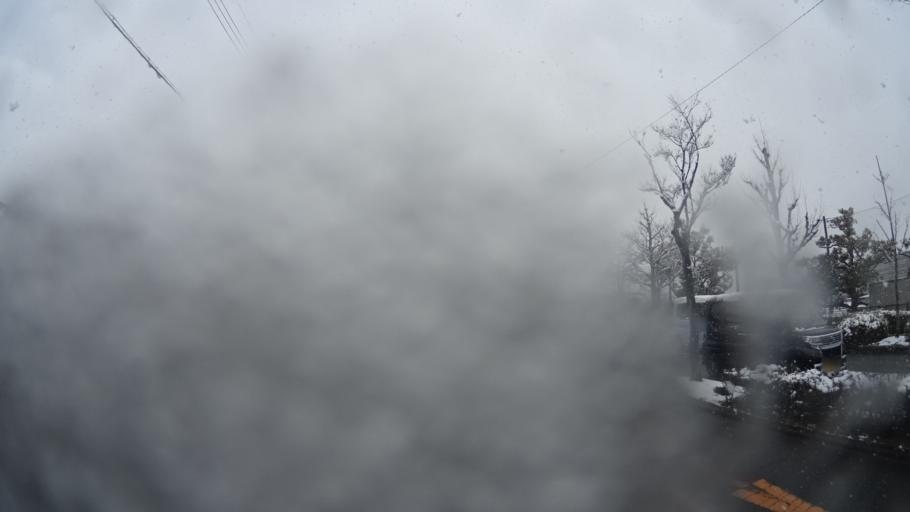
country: JP
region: Kyoto
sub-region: Kyoto-shi
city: Kamigyo-ku
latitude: 35.0645
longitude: 135.7863
